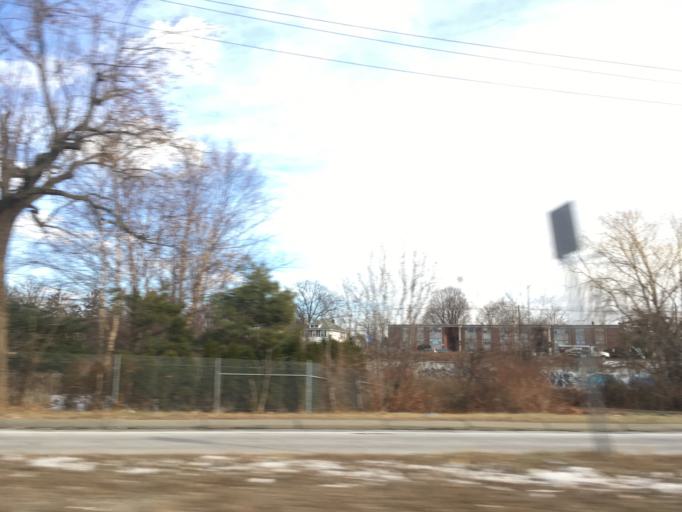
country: US
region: Rhode Island
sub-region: Providence County
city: Cranston
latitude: 41.7856
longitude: -71.4327
